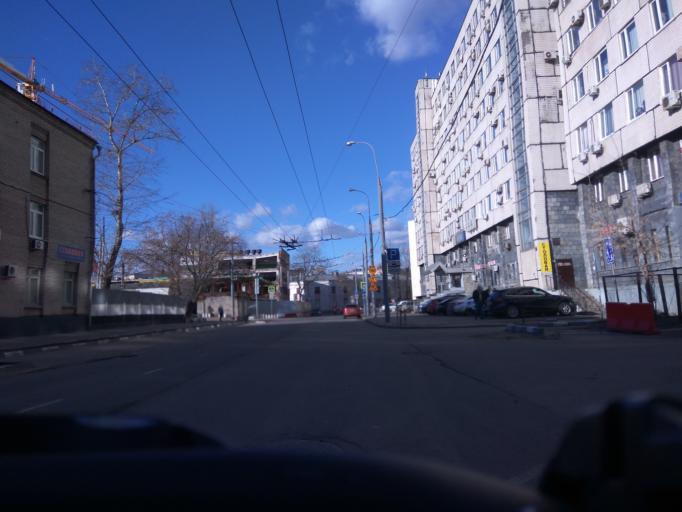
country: RU
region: Moscow
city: Mar'ina Roshcha
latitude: 55.8117
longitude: 37.6315
